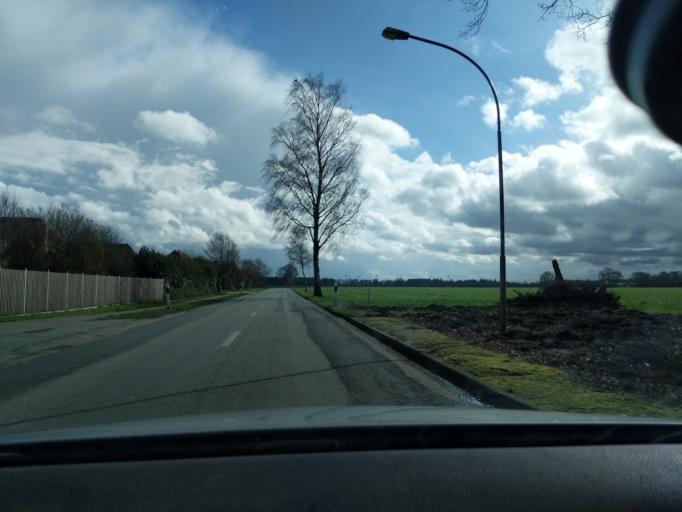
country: DE
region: Lower Saxony
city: Heinbockel
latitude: 53.5724
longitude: 9.3271
